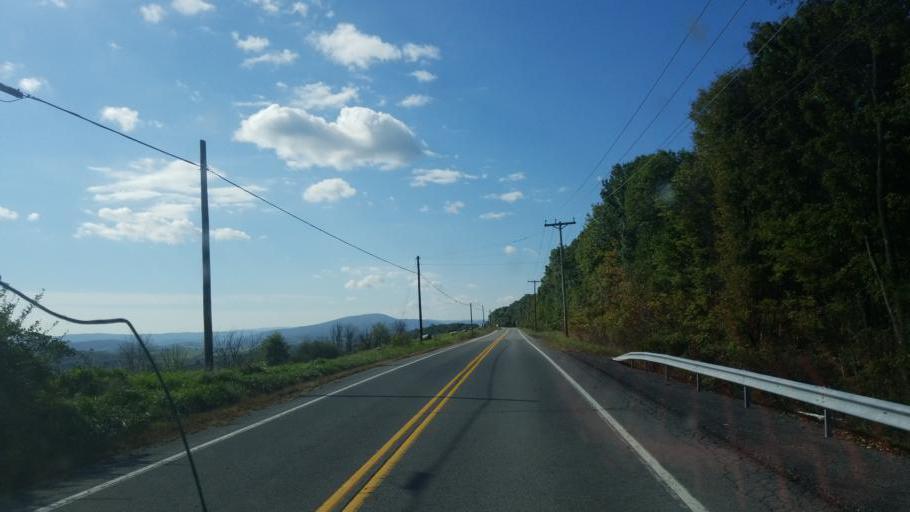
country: US
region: Pennsylvania
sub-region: Bedford County
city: Bedford
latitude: 40.1416
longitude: -78.5143
